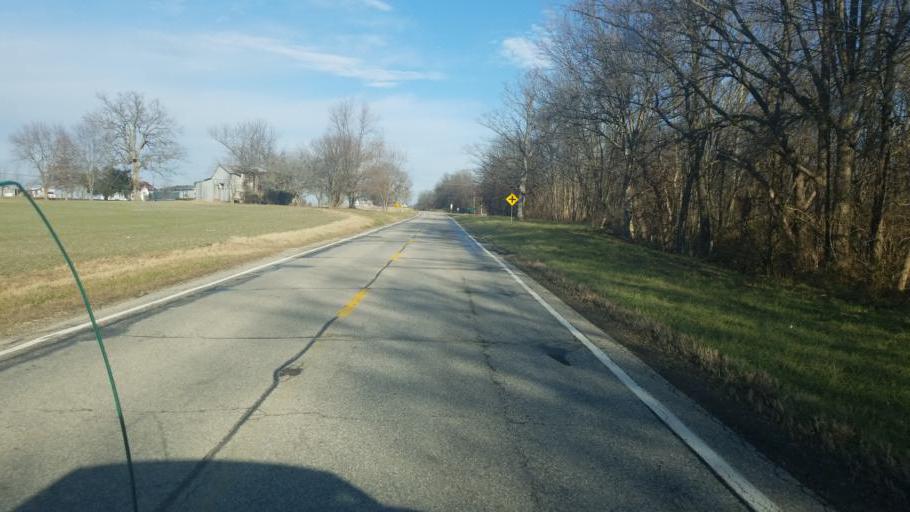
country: US
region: Illinois
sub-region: Wabash County
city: Mount Carmel
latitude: 38.3486
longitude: -87.8737
